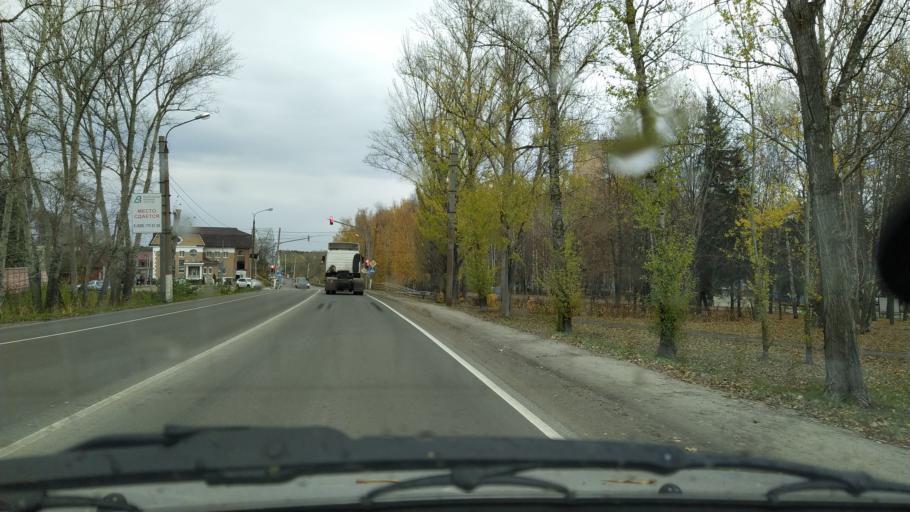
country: RU
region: Moskovskaya
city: Voskresensk
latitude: 55.3182
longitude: 38.6496
